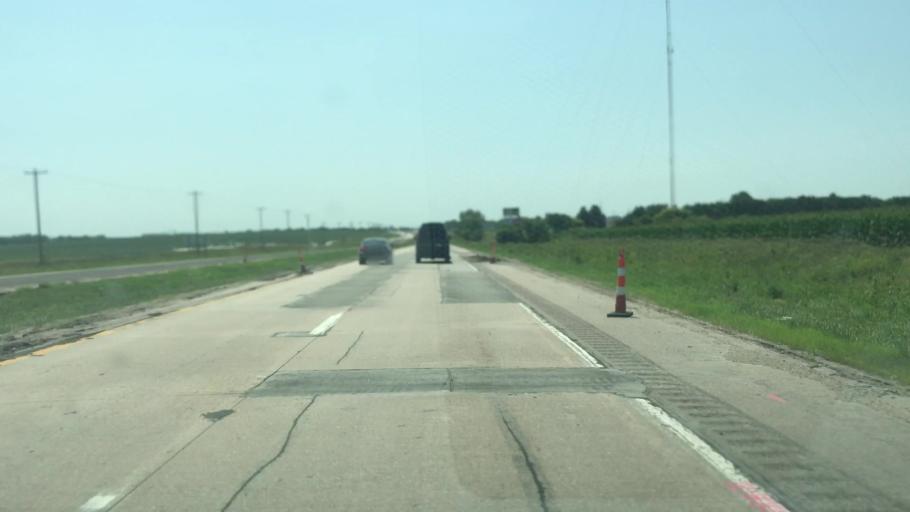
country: US
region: Nebraska
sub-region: Adams County
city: Hastings
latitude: 40.6529
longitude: -98.3825
